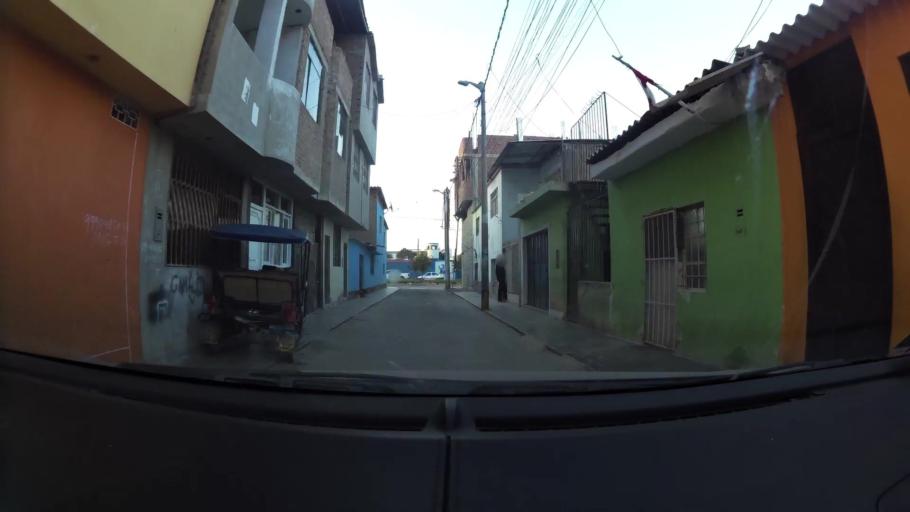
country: PE
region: Lambayeque
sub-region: Provincia de Chiclayo
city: Santa Rosa
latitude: -6.7640
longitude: -79.8329
